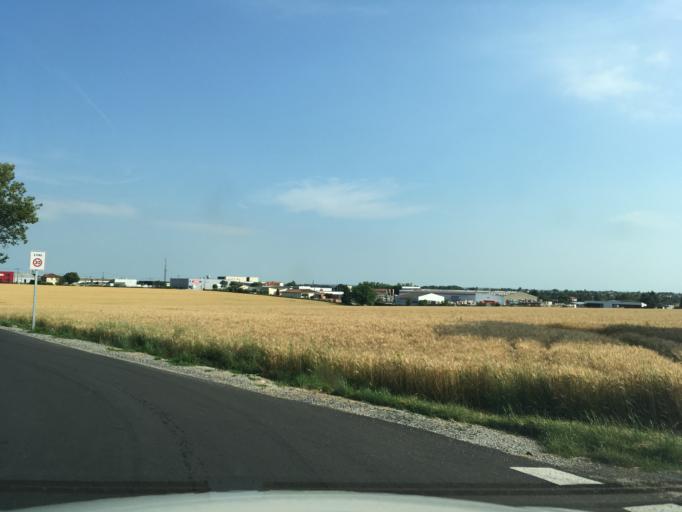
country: FR
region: Poitou-Charentes
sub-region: Departement des Deux-Sevres
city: Niort
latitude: 46.3414
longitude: -0.4241
